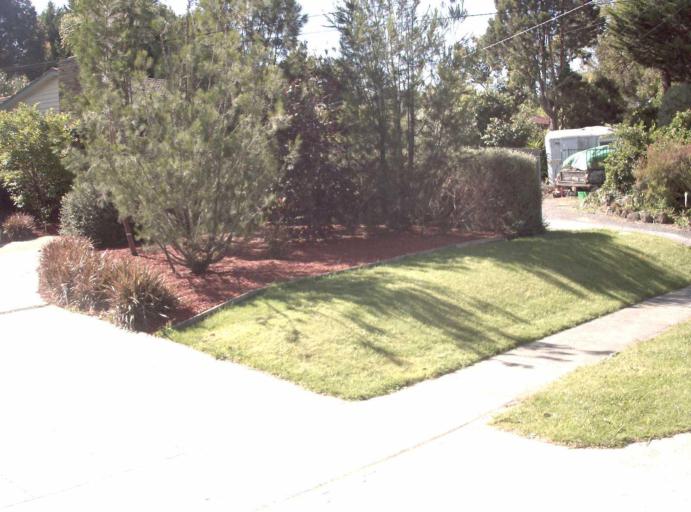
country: AU
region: Victoria
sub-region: Knox
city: Bayswater
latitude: -37.8657
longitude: 145.2634
